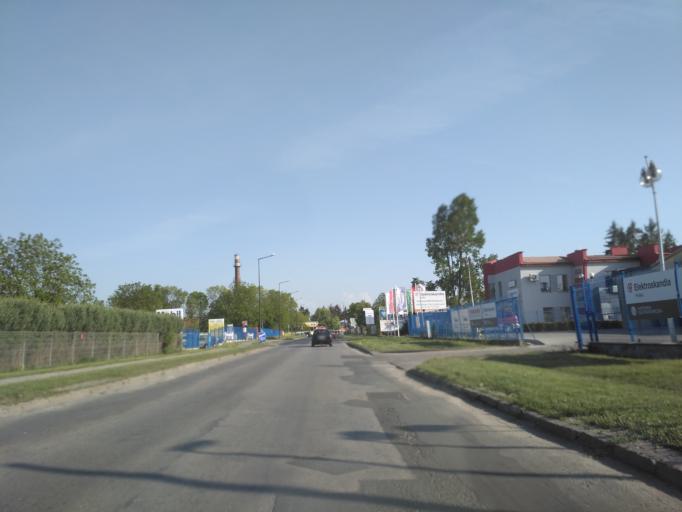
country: PL
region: Lublin Voivodeship
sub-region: Powiat lubelski
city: Lublin
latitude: 51.2075
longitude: 22.5632
